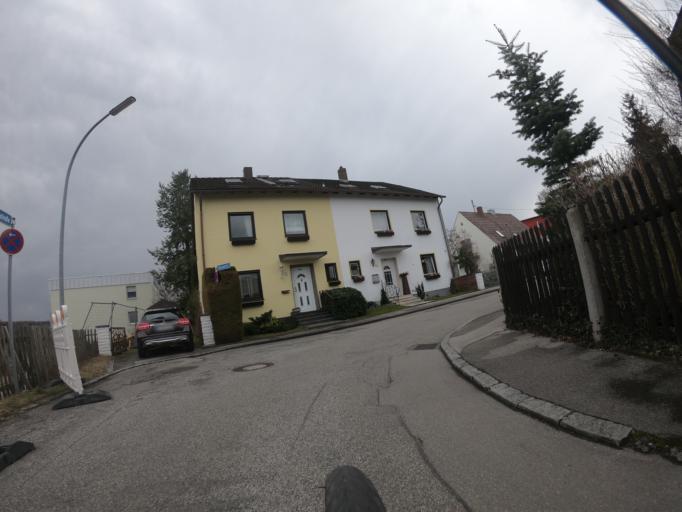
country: DE
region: Bavaria
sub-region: Upper Bavaria
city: Fuerstenfeldbruck
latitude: 48.1726
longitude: 11.2394
